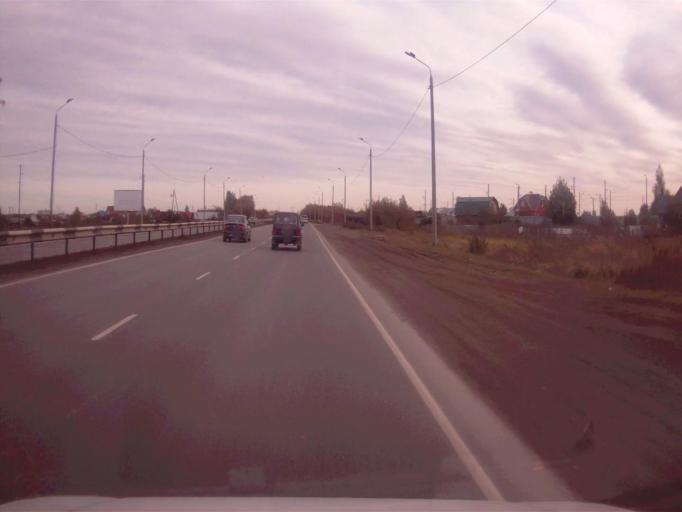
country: RU
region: Chelyabinsk
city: Novosineglazovskiy
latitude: 55.0450
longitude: 61.4210
